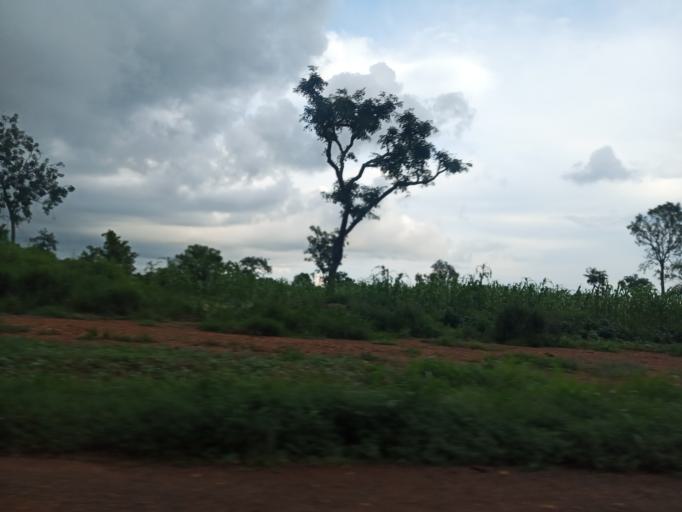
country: TG
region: Centrale
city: Sotouboua
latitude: 8.5937
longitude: 0.9959
